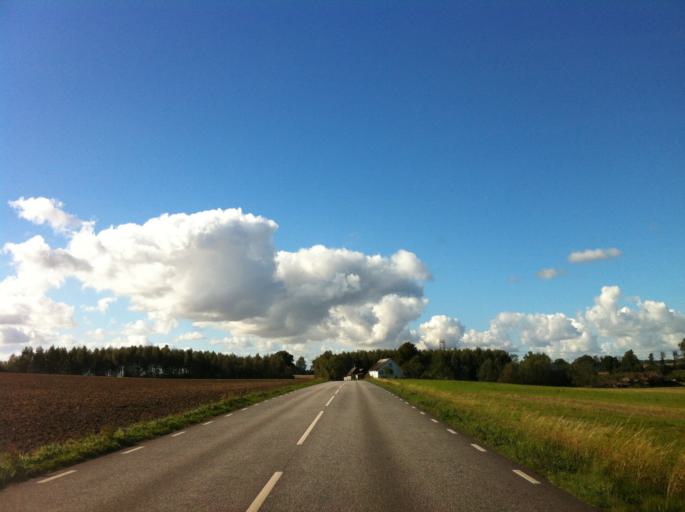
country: SE
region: Skane
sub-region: Hoors Kommun
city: Loberod
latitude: 55.7419
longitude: 13.4260
